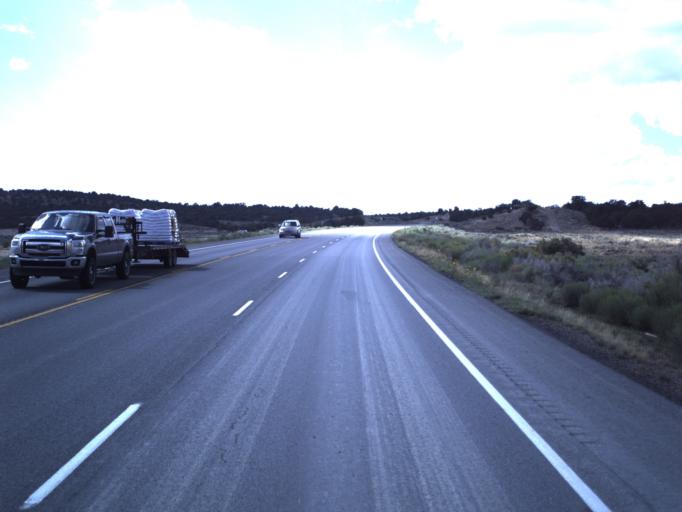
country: US
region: Utah
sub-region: Duchesne County
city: Duchesne
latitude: 40.1741
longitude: -110.5910
